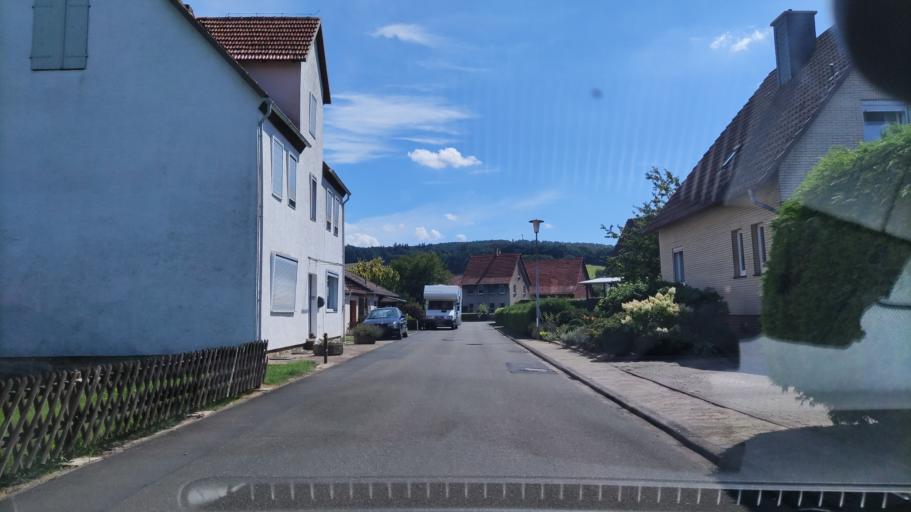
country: DE
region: Lower Saxony
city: Bodenfelde
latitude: 51.6250
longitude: 9.5619
